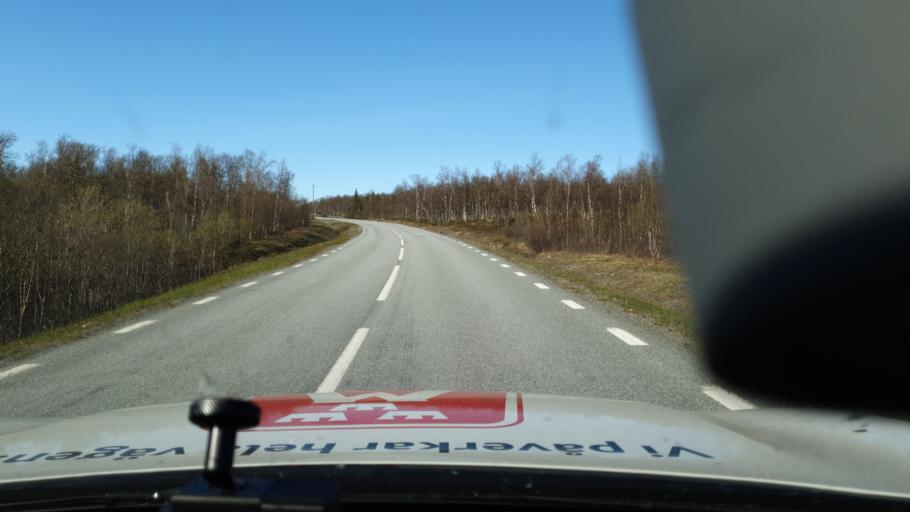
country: NO
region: Nordland
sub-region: Rana
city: Mo i Rana
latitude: 65.9752
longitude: 15.0633
